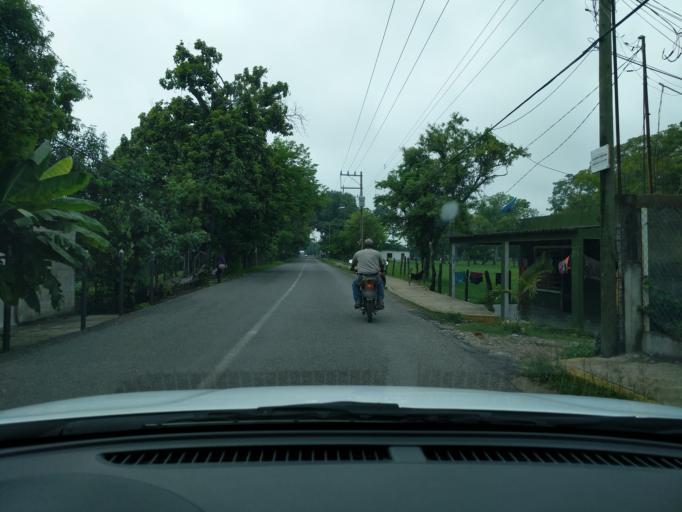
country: MX
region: Tabasco
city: Villahermosa
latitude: 17.9543
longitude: -92.9650
